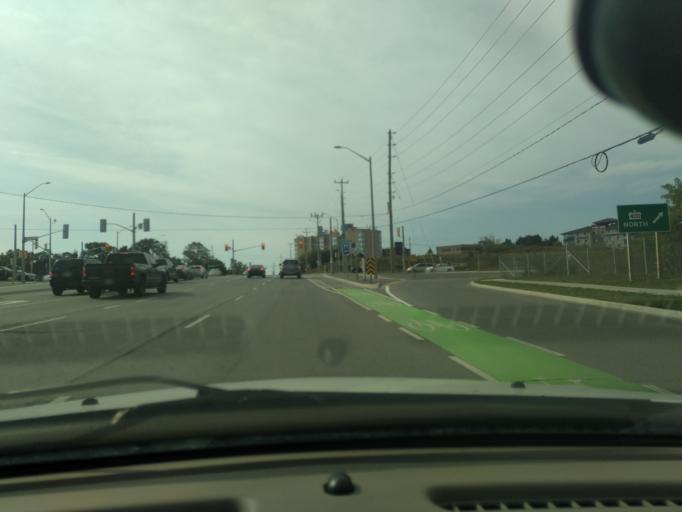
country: CA
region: Ontario
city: Barrie
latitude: 44.4130
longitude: -79.6733
